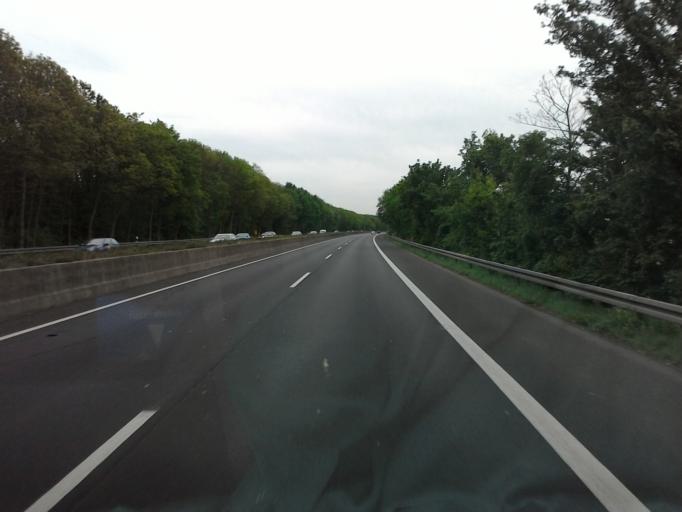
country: DE
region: North Rhine-Westphalia
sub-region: Regierungsbezirk Dusseldorf
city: Dormagen
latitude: 51.0668
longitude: 6.8308
